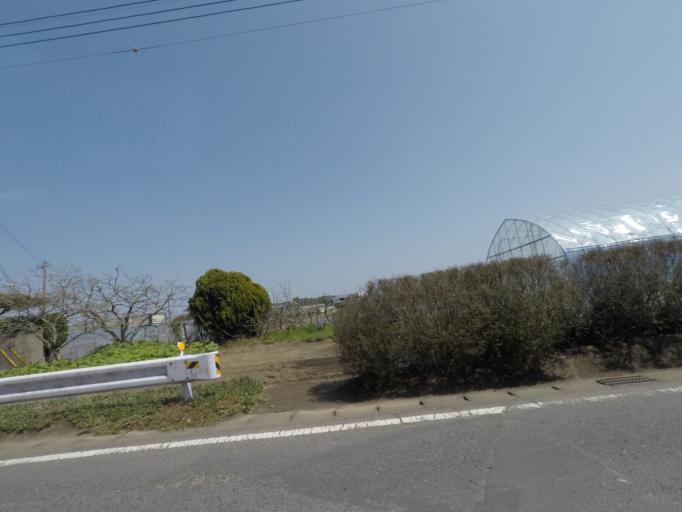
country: JP
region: Chiba
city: Yokaichiba
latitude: 35.6751
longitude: 140.4689
